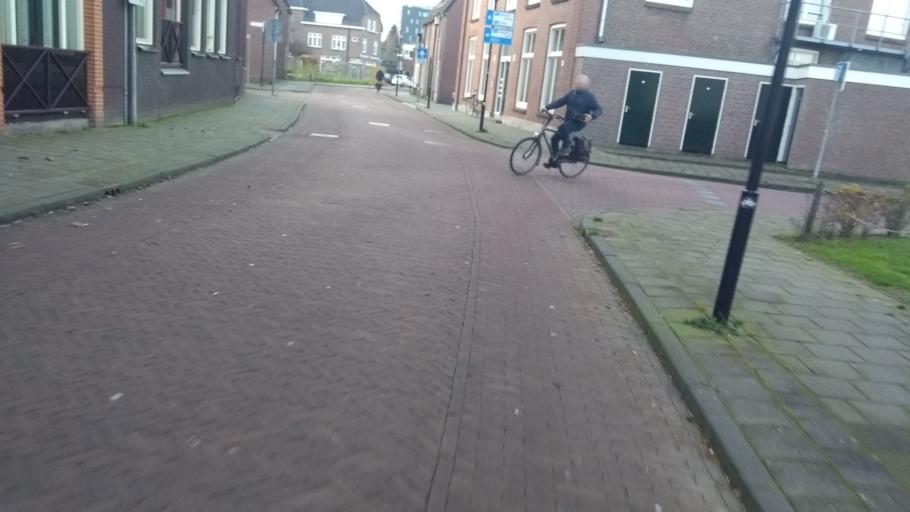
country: NL
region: Overijssel
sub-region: Gemeente Almelo
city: Almelo
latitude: 52.3530
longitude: 6.6649
